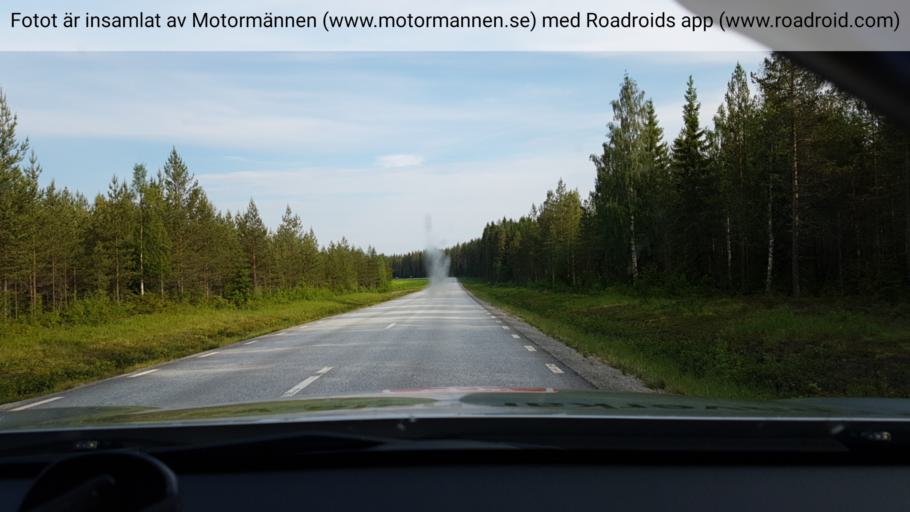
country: SE
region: Vaesterbotten
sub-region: Vindelns Kommun
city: Vindeln
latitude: 64.0964
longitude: 19.6075
